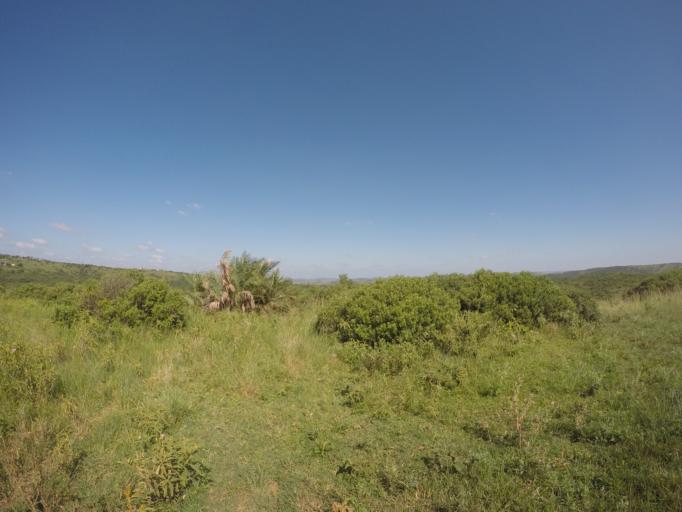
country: ZA
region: KwaZulu-Natal
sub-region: uThungulu District Municipality
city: Empangeni
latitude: -28.5705
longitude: 31.7005
